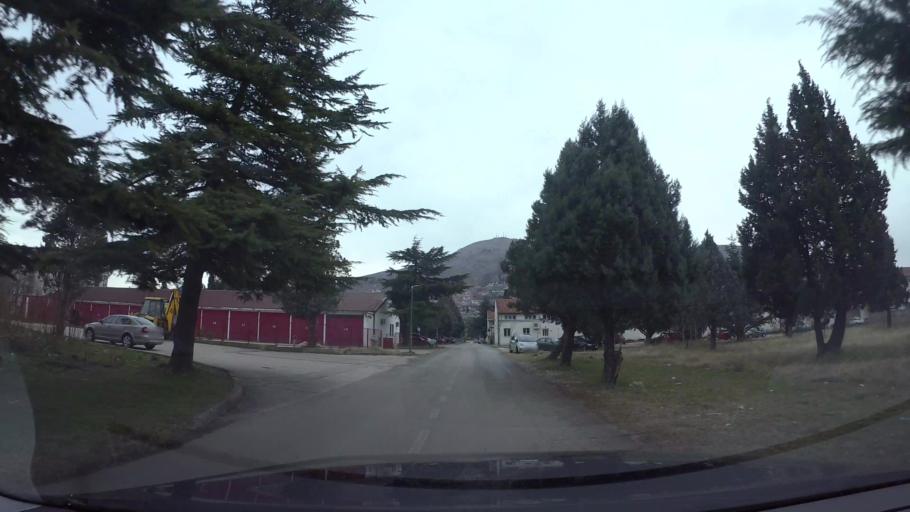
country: BA
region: Federation of Bosnia and Herzegovina
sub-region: Hercegovacko-Bosanski Kanton
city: Mostar
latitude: 43.3556
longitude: 17.8087
